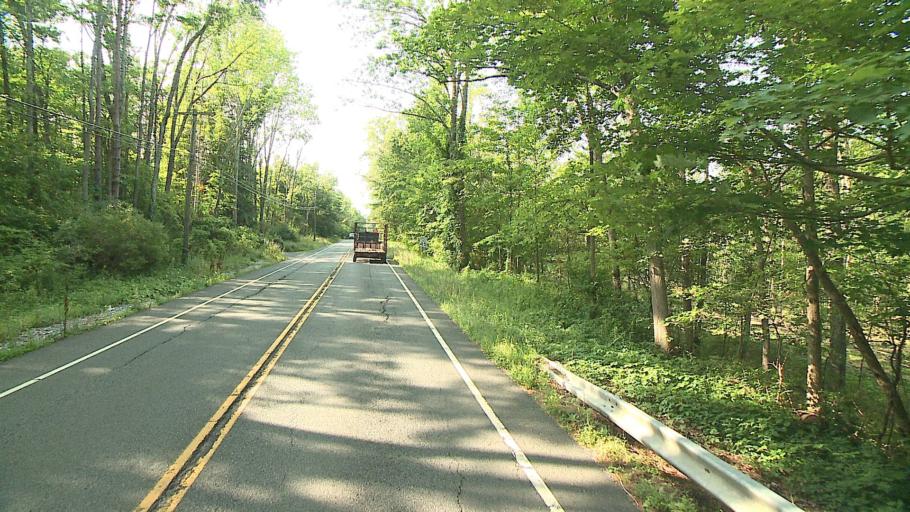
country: US
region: Connecticut
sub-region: Litchfield County
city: Canaan
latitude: 41.9510
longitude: -73.3600
